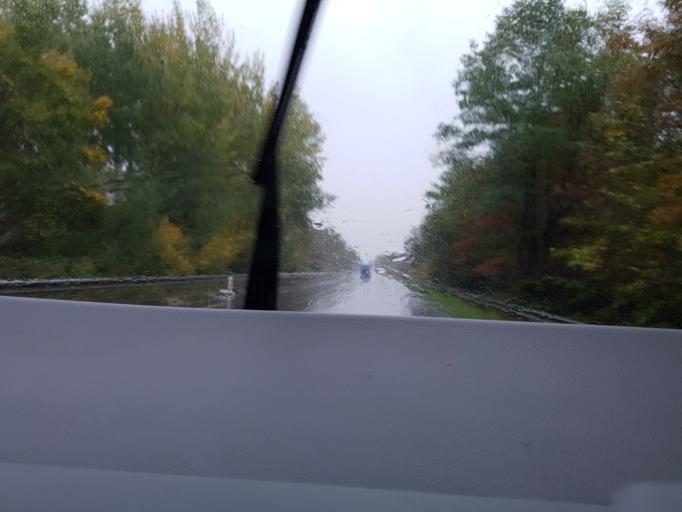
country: FR
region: Aquitaine
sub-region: Departement de la Gironde
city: Saint-Louis-de-Montferrand
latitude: 44.9603
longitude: -0.5037
